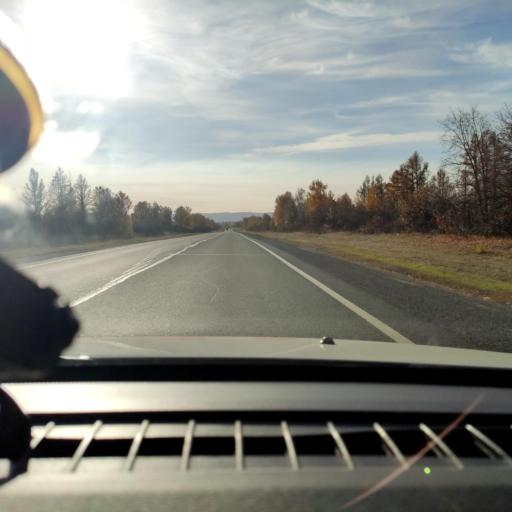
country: RU
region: Samara
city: Volzhskiy
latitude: 53.4738
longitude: 50.1198
